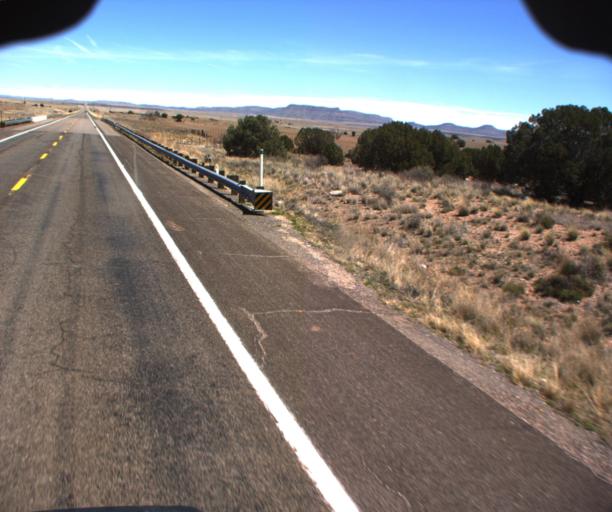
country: US
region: Arizona
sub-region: Mohave County
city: Peach Springs
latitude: 35.4608
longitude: -113.6129
